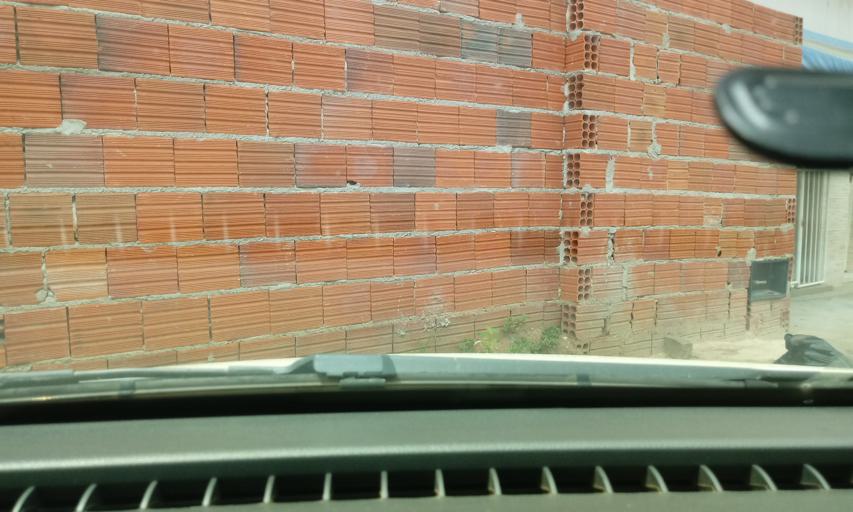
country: BR
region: Bahia
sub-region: Guanambi
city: Guanambi
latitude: -14.2292
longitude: -42.7798
